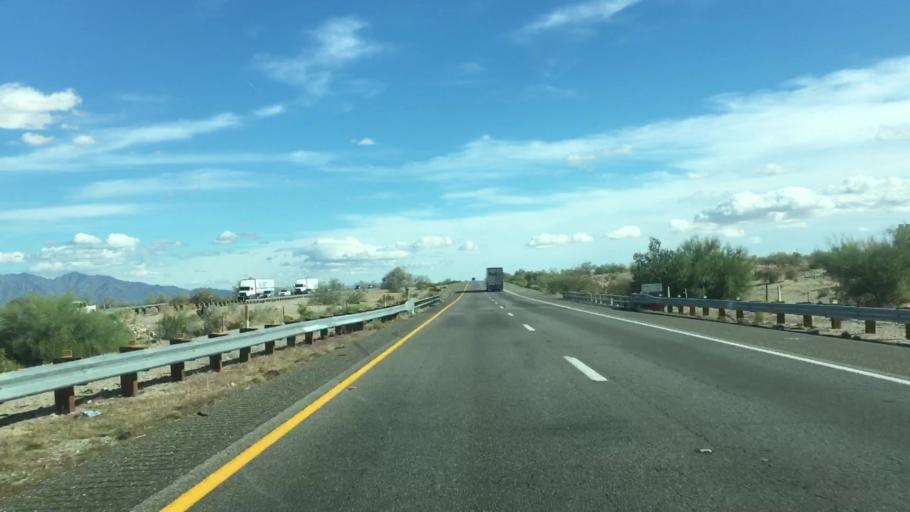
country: US
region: California
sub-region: Imperial County
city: Niland
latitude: 33.7062
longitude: -115.3458
